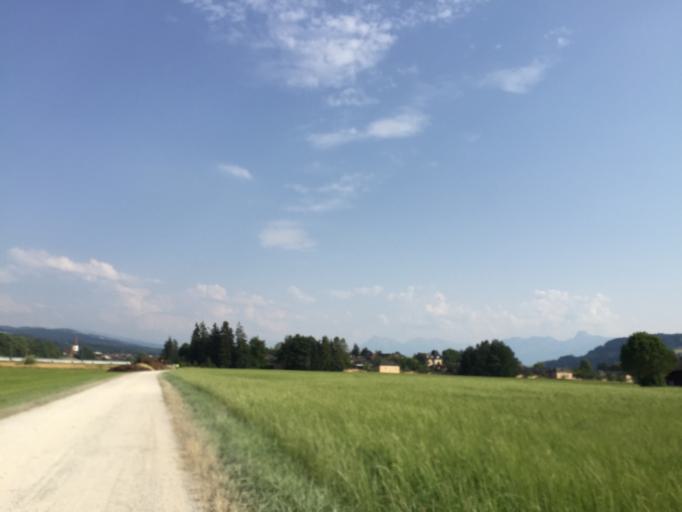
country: CH
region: Bern
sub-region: Bern-Mittelland District
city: Rubigen
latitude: 46.8857
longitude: 7.5503
